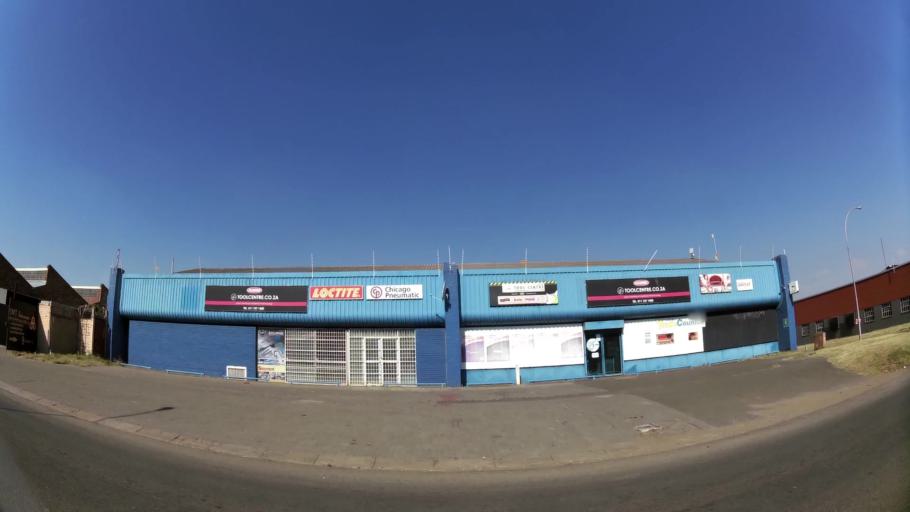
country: ZA
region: Gauteng
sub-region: Ekurhuleni Metropolitan Municipality
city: Benoni
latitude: -26.2043
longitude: 28.3015
